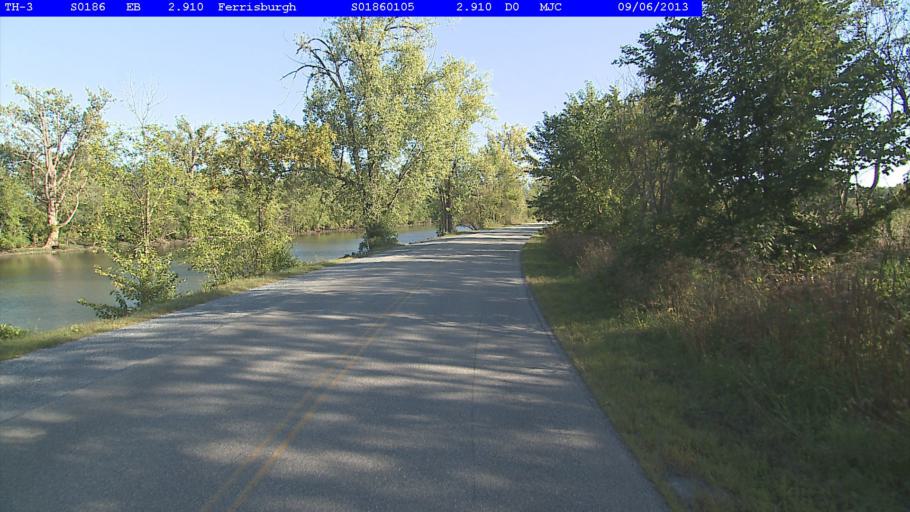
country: US
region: Vermont
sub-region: Addison County
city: Vergennes
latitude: 44.1845
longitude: -73.3104
